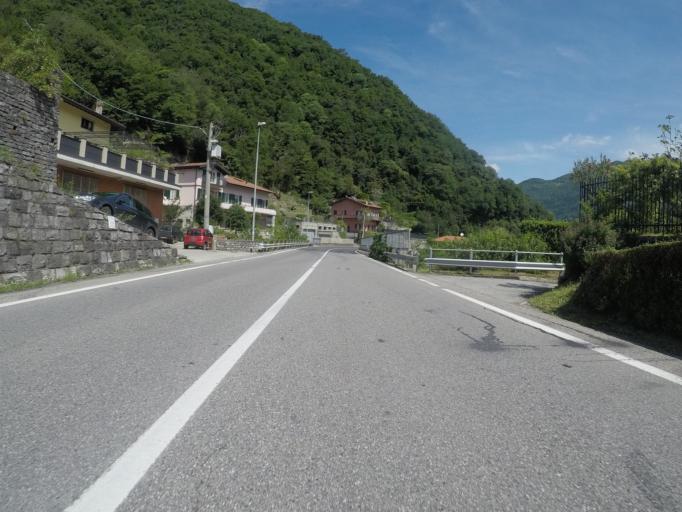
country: IT
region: Lombardy
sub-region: Provincia di Como
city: Laglio
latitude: 45.8862
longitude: 9.1408
